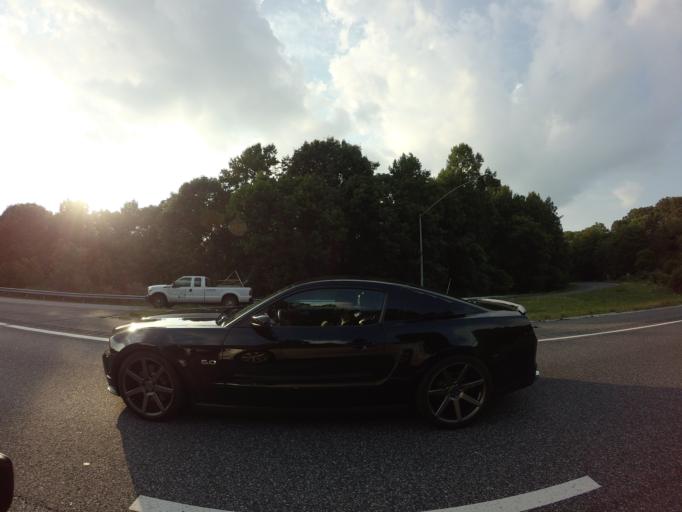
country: US
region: Maryland
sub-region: Howard County
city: Savage
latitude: 39.1575
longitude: -76.8327
